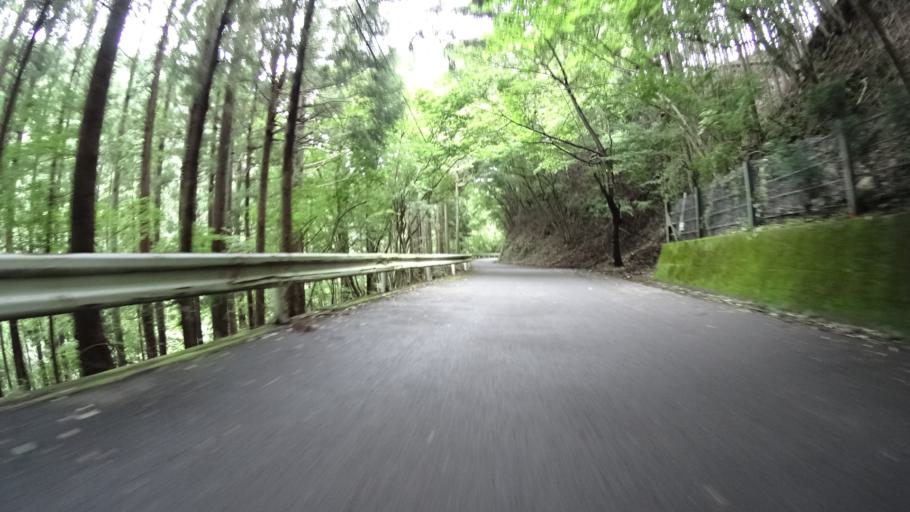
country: JP
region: Kanagawa
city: Hadano
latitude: 35.4971
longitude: 139.2223
